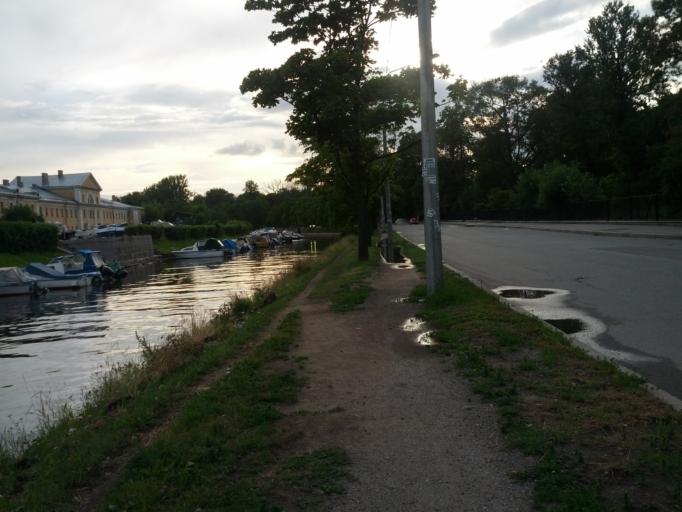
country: RU
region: St.-Petersburg
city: Petrogradka
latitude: 59.9678
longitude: 30.3298
